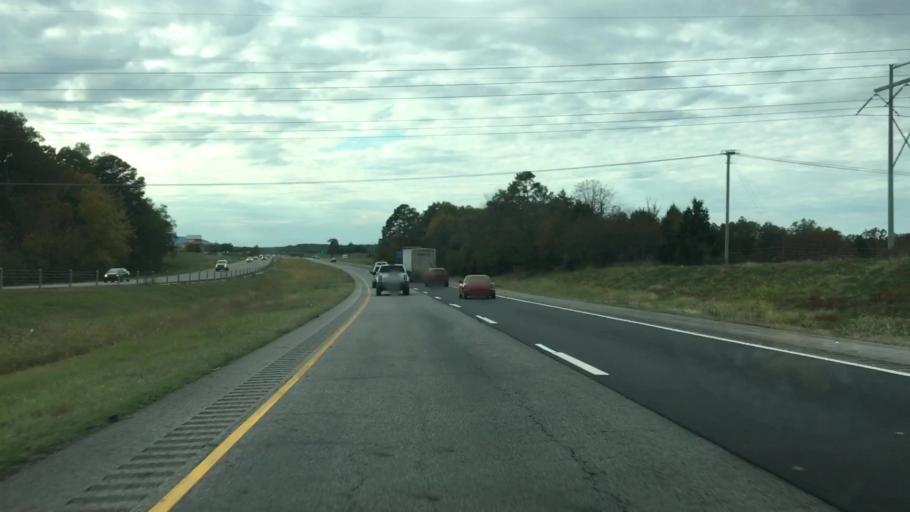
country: US
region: Arkansas
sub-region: Conway County
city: Morrilton
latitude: 35.1741
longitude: -92.7052
